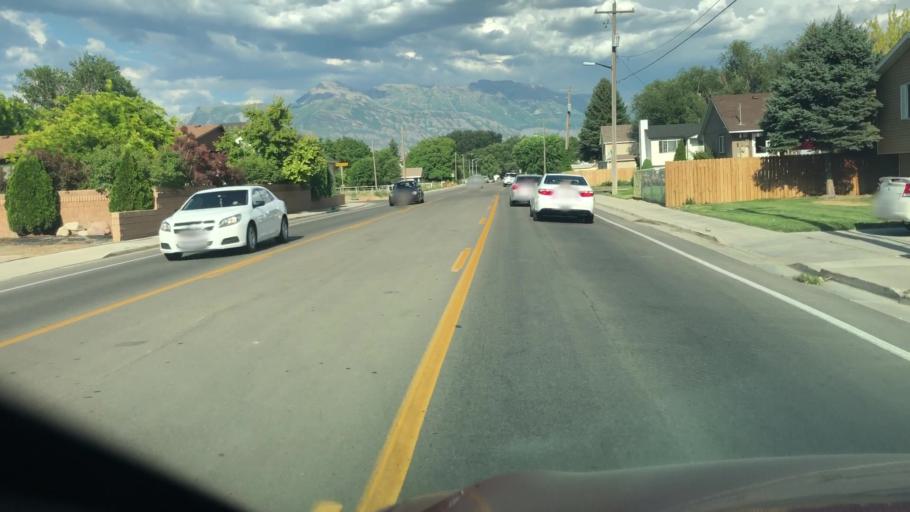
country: US
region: Utah
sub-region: Utah County
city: Lehi
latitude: 40.3872
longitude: -111.8622
